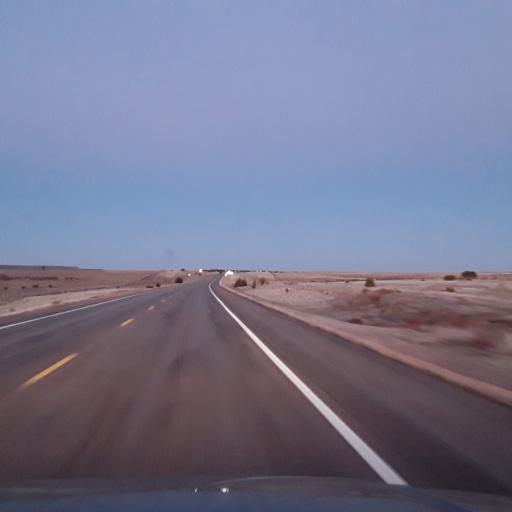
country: US
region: New Mexico
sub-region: Guadalupe County
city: Santa Rosa
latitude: 34.7423
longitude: -105.0222
